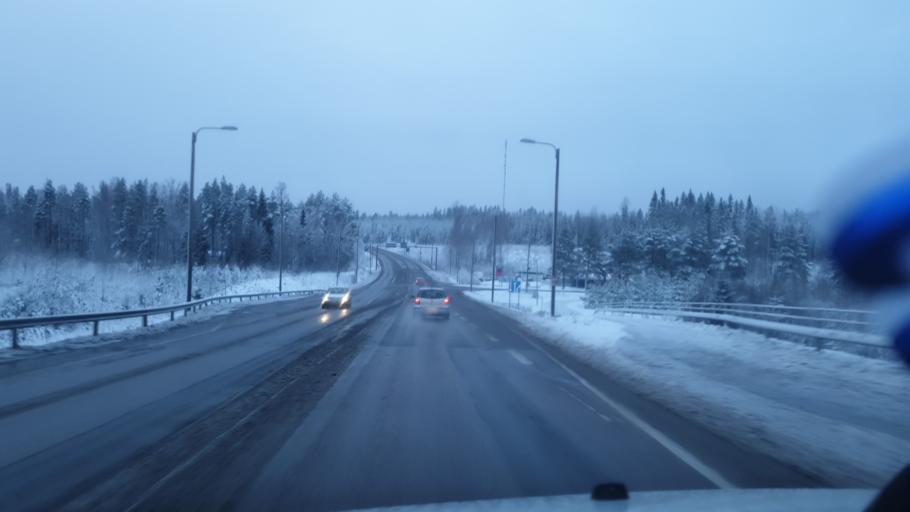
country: FI
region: Central Finland
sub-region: Saarijaervi-Viitasaari
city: Viitasaari
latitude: 63.0415
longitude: 25.8149
